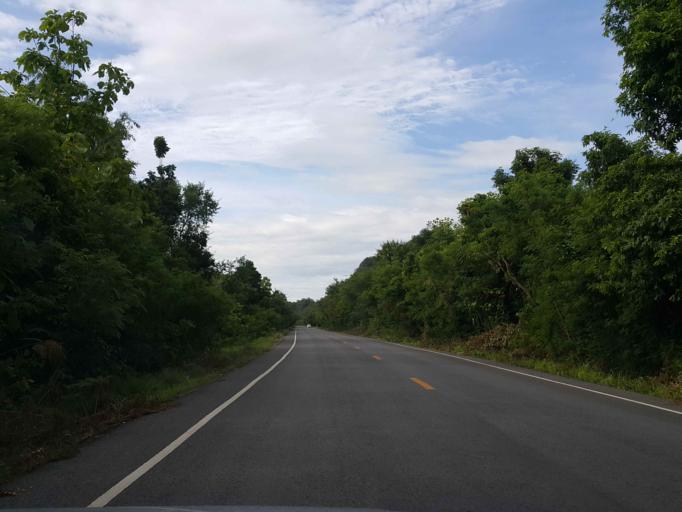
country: TH
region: Sukhothai
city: Thung Saliam
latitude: 17.2878
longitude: 99.5270
